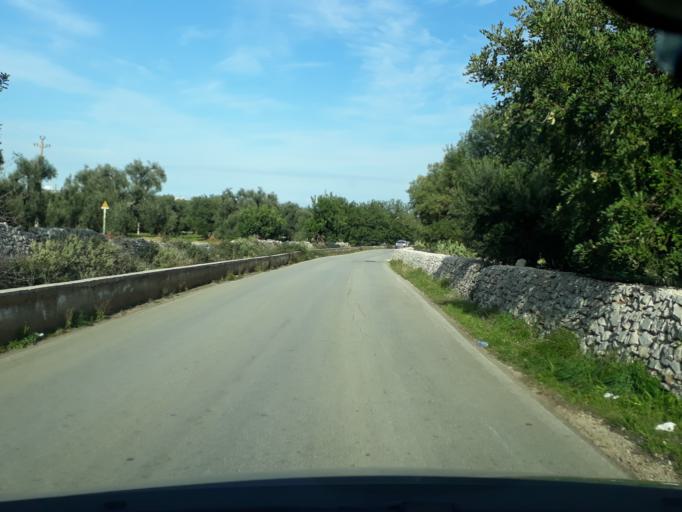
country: IT
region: Apulia
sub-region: Provincia di Brindisi
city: Fasano
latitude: 40.8204
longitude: 17.3582
